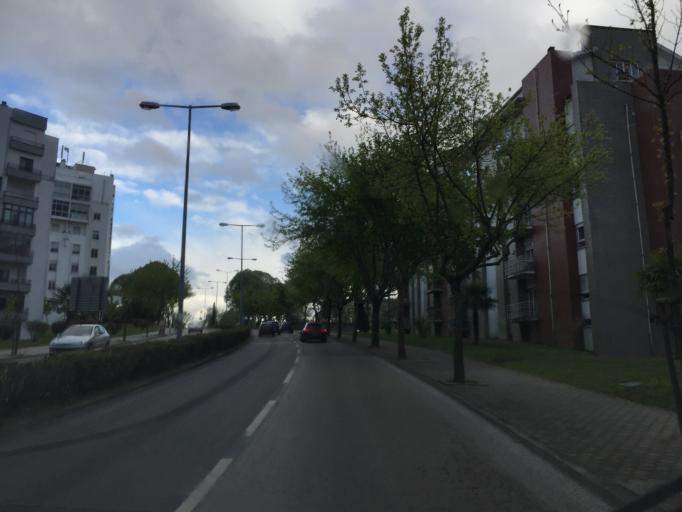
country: PT
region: Viseu
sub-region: Viseu
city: Viseu
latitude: 40.6511
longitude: -7.9211
